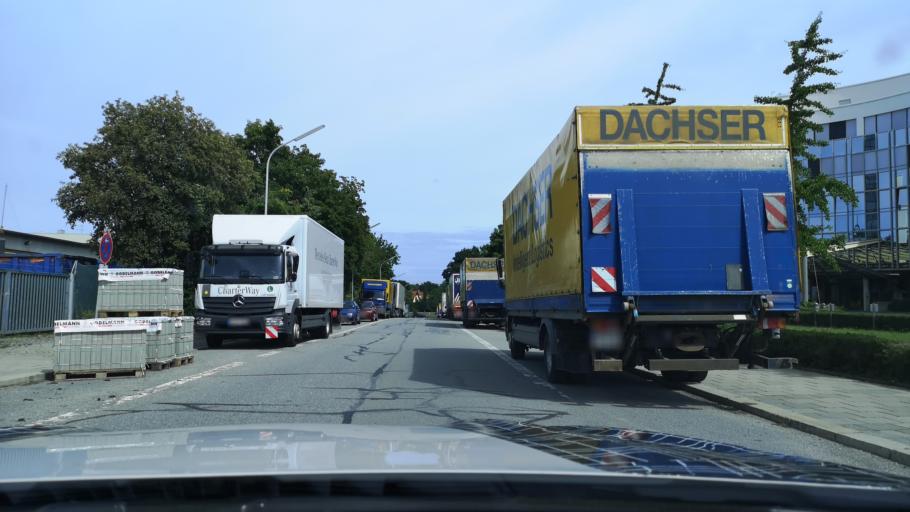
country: DE
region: Bavaria
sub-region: Upper Bavaria
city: Bogenhausen
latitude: 48.1367
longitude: 11.6397
